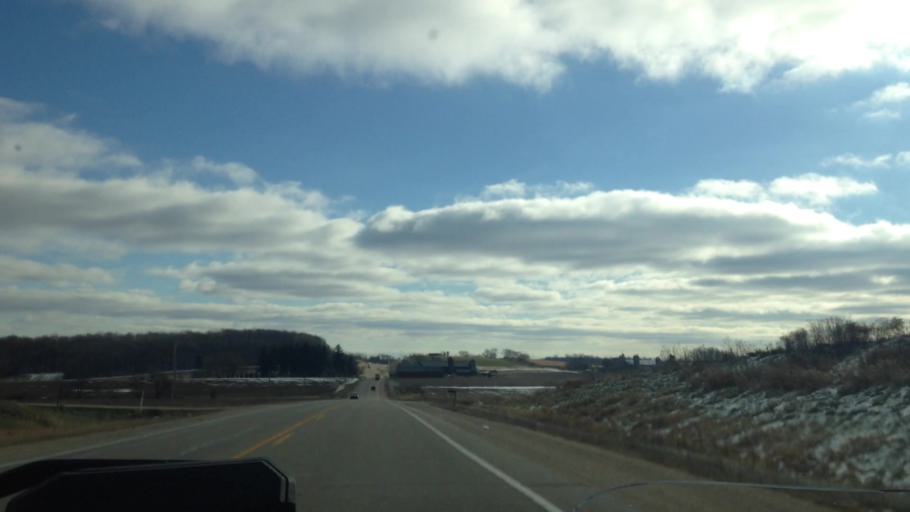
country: US
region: Wisconsin
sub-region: Dodge County
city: Theresa
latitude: 43.4389
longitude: -88.4671
